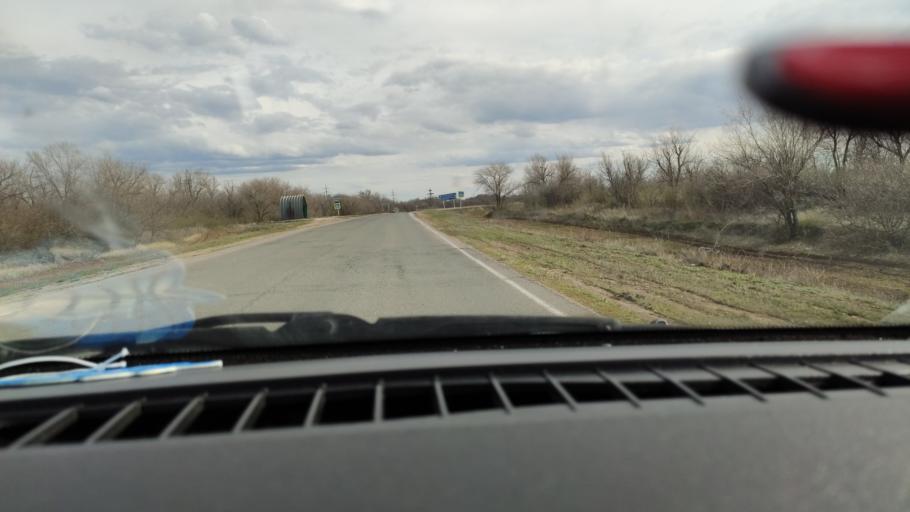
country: RU
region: Saratov
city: Rovnoye
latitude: 50.9409
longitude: 46.1263
